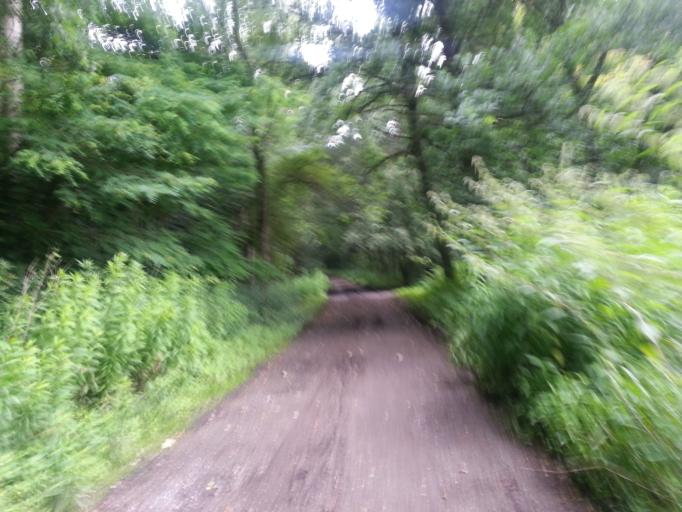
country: DE
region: North Rhine-Westphalia
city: Oer-Erkenschwick
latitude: 51.6992
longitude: 7.2577
